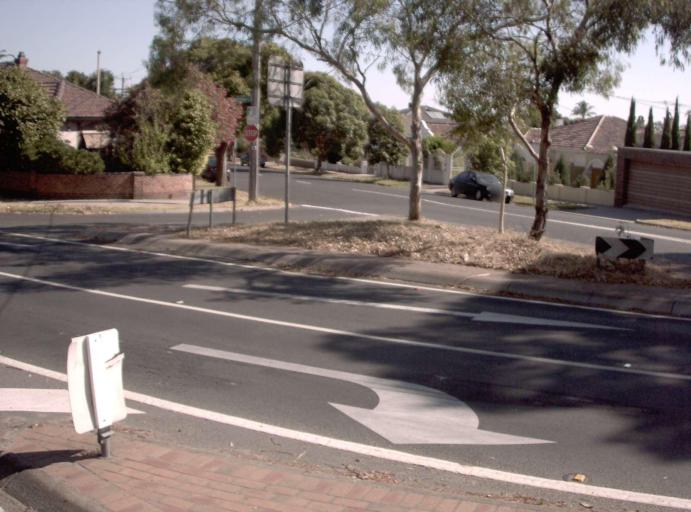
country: AU
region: Victoria
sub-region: Stonnington
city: Malvern East
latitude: -37.8814
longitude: 145.0348
